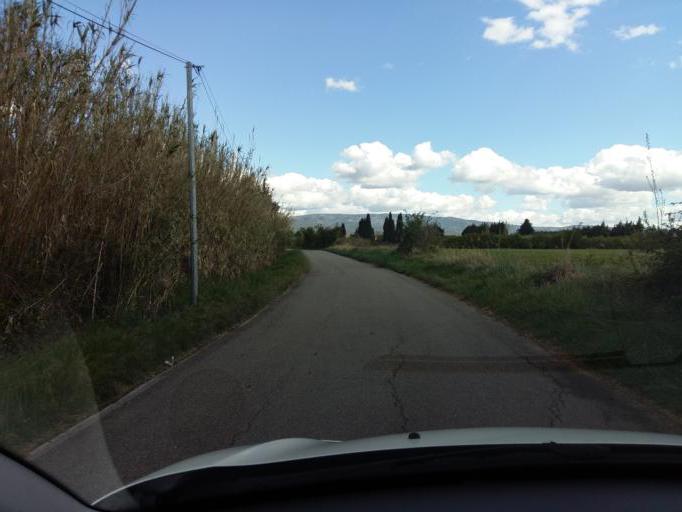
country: FR
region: Provence-Alpes-Cote d'Azur
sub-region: Departement du Vaucluse
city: Le Thor
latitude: 43.9308
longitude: 5.0123
